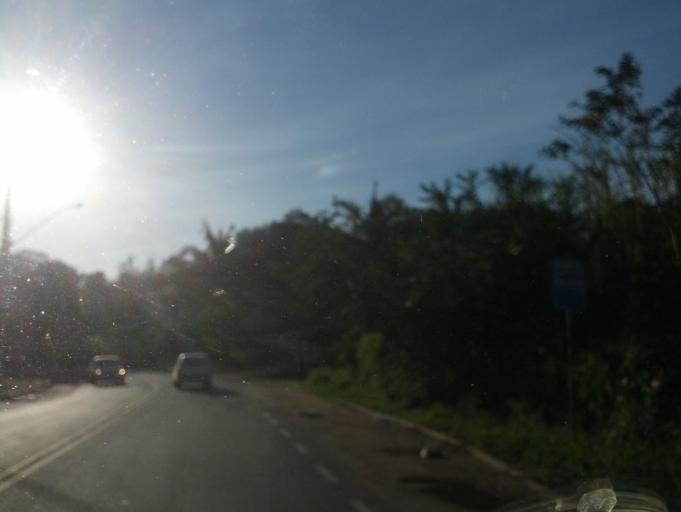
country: BR
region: Santa Catarina
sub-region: Indaial
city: Indaial
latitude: -26.8895
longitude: -49.2146
